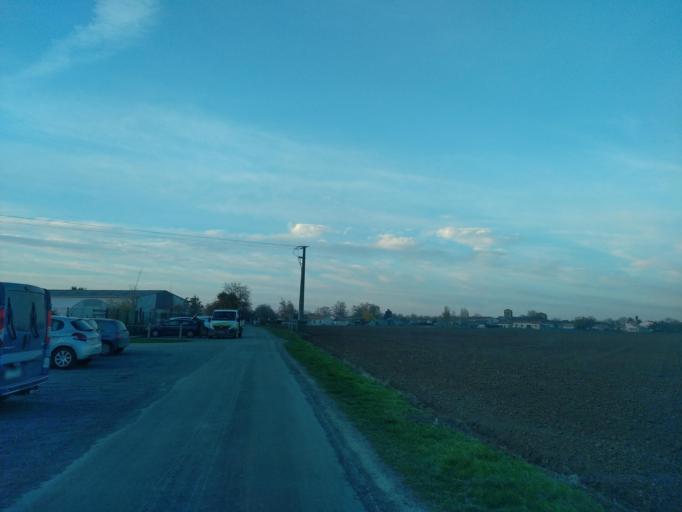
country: FR
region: Pays de la Loire
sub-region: Departement de la Vendee
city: Maillezais
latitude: 46.3658
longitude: -0.7394
